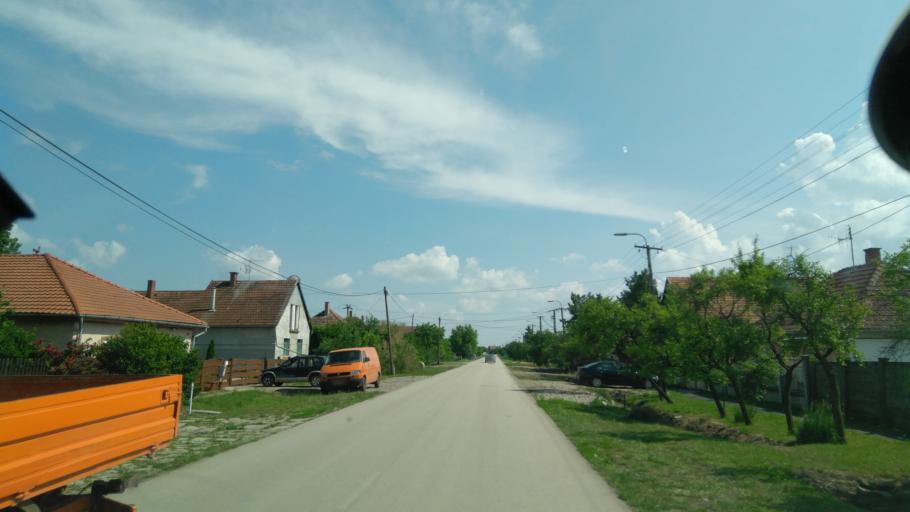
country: HU
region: Bekes
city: Doboz
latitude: 46.7375
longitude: 21.2367
